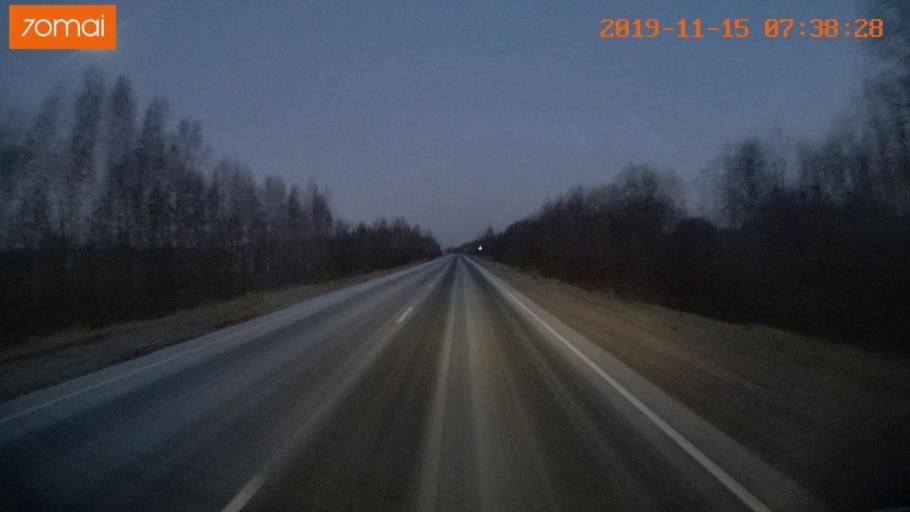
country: RU
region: Vologda
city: Sheksna
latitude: 58.7575
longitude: 38.4009
